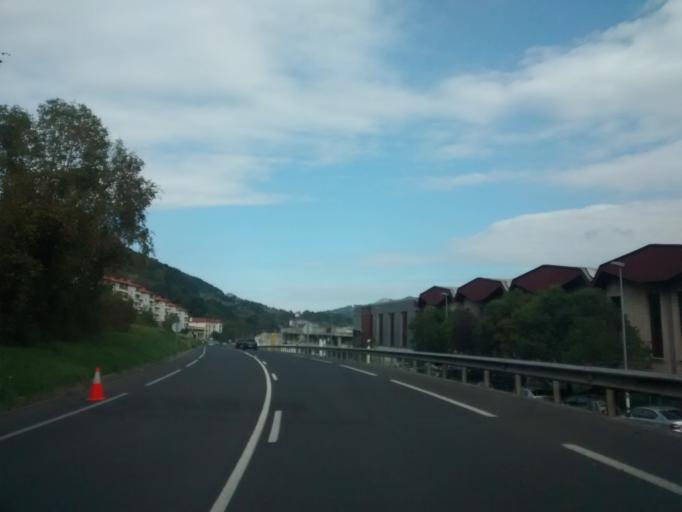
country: ES
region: Basque Country
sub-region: Provincia de Guipuzcoa
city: Elgoibar
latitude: 43.2052
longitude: -2.4247
